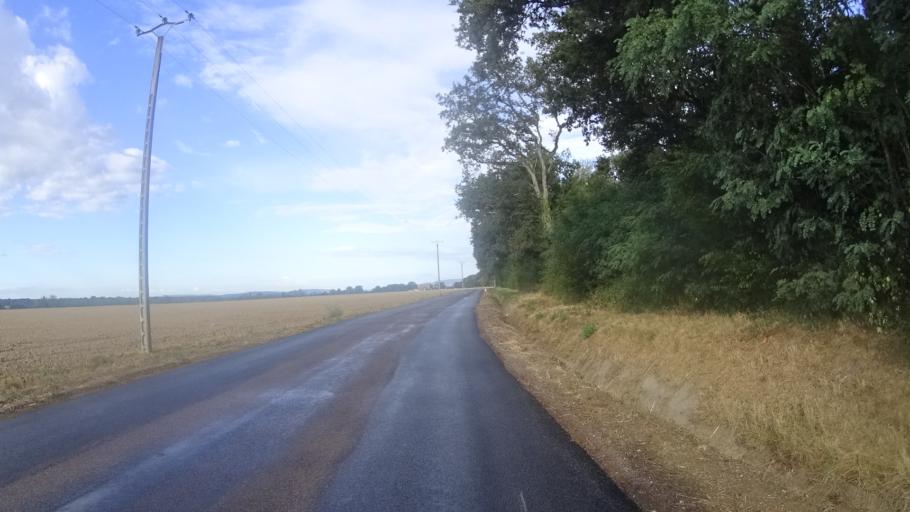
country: FR
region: Bourgogne
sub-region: Departement de Saone-et-Loire
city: Demigny
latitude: 46.9592
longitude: 4.9022
